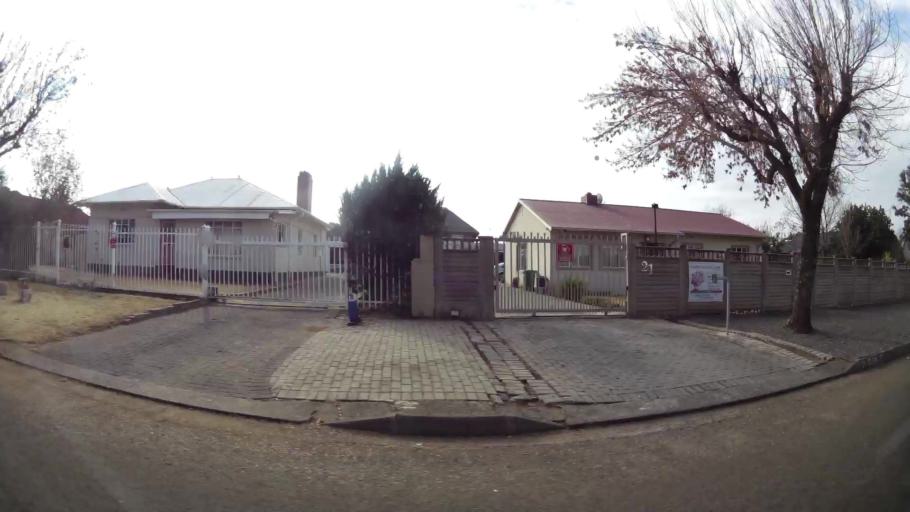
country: ZA
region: Orange Free State
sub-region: Mangaung Metropolitan Municipality
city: Bloemfontein
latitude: -29.0812
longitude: 26.2417
